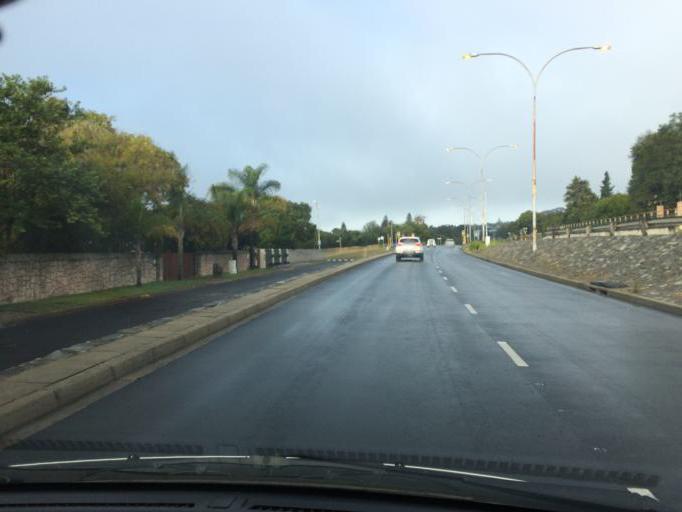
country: ZA
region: Western Cape
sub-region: City of Cape Town
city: Kraaifontein
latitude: -33.8415
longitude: 18.6479
